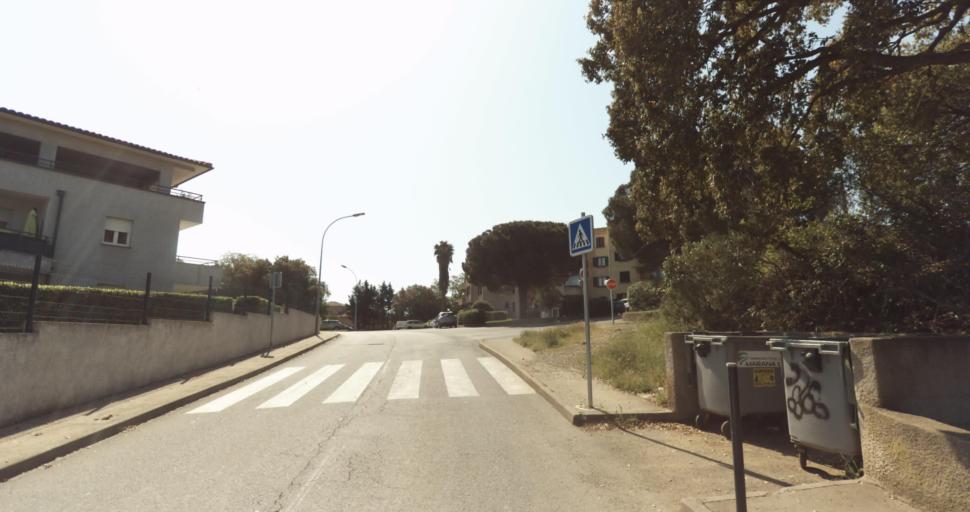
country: FR
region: Corsica
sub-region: Departement de la Haute-Corse
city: Biguglia
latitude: 42.6242
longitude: 9.4336
